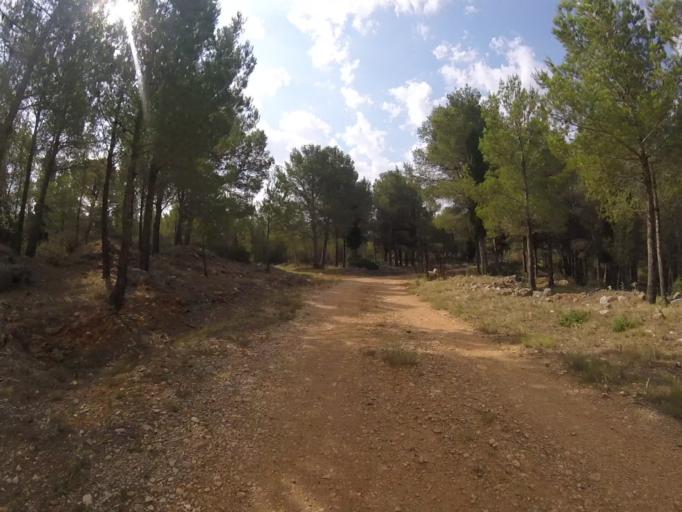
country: ES
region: Valencia
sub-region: Provincia de Castello
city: Alcala de Xivert
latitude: 40.3636
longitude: 0.2029
